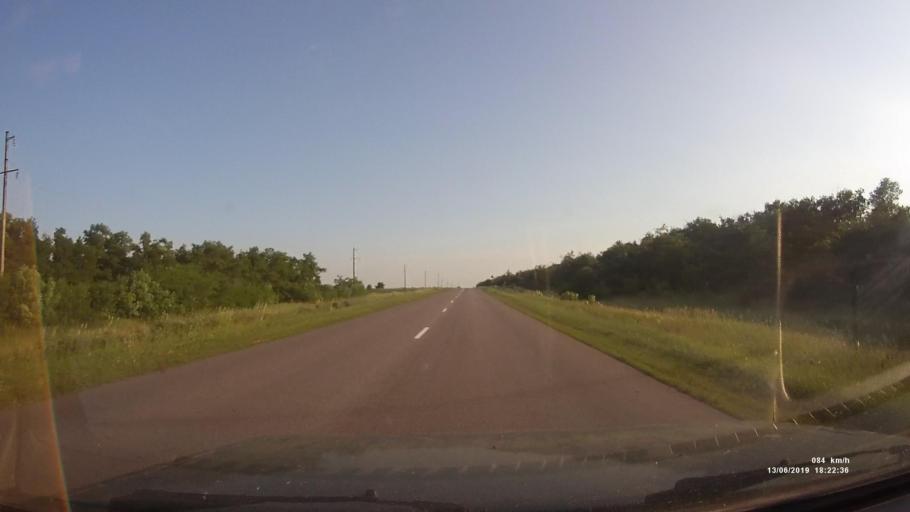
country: RU
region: Rostov
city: Kazanskaya
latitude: 49.8566
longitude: 41.2772
